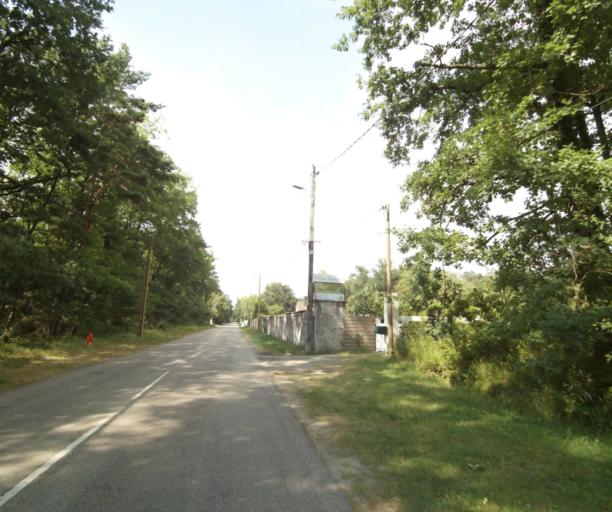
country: FR
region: Ile-de-France
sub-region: Departement de Seine-et-Marne
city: Arbonne-la-Foret
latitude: 48.4007
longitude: 2.5600
